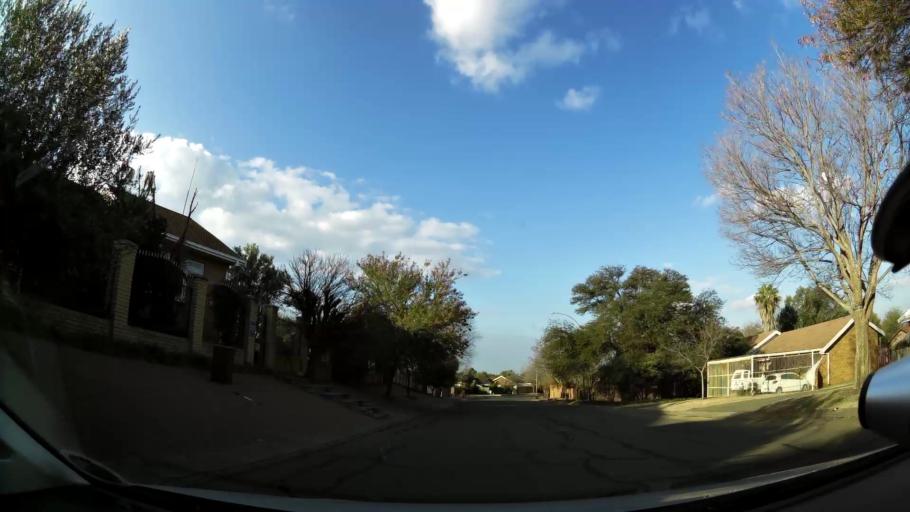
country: ZA
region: Orange Free State
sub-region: Mangaung Metropolitan Municipality
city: Bloemfontein
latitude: -29.1548
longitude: 26.1792
